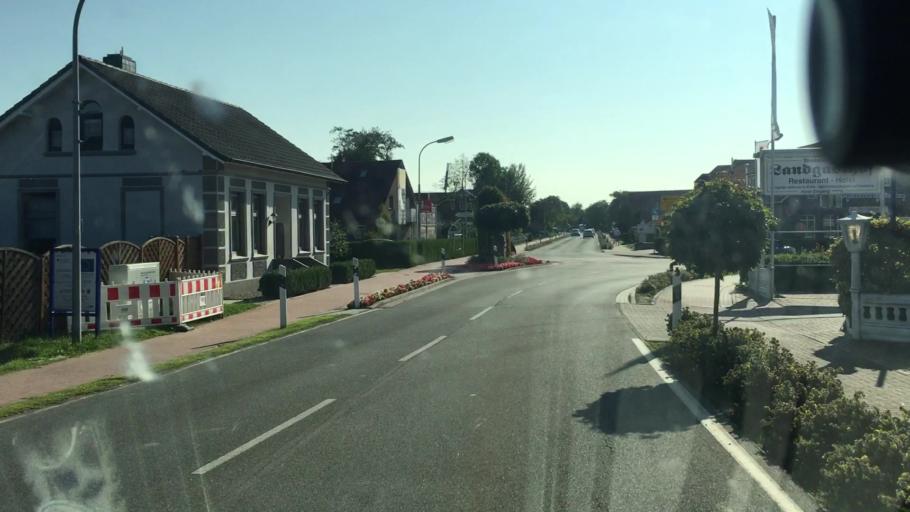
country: DE
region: Lower Saxony
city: Werdum
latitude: 53.6604
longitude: 7.7150
